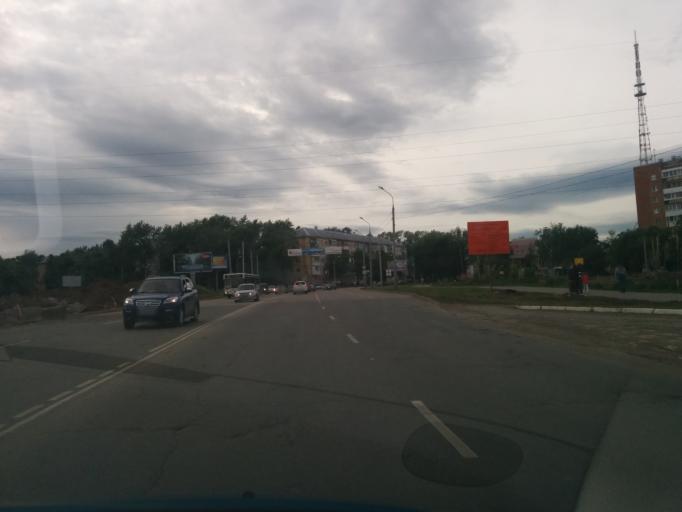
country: RU
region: Perm
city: Perm
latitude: 58.0088
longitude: 56.2960
